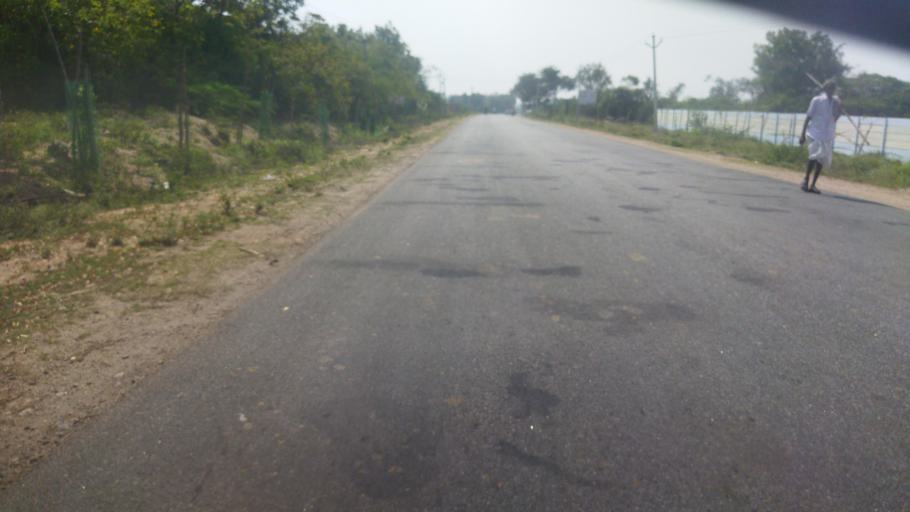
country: IN
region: Telangana
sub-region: Nalgonda
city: Nalgonda
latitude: 17.0945
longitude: 79.2857
